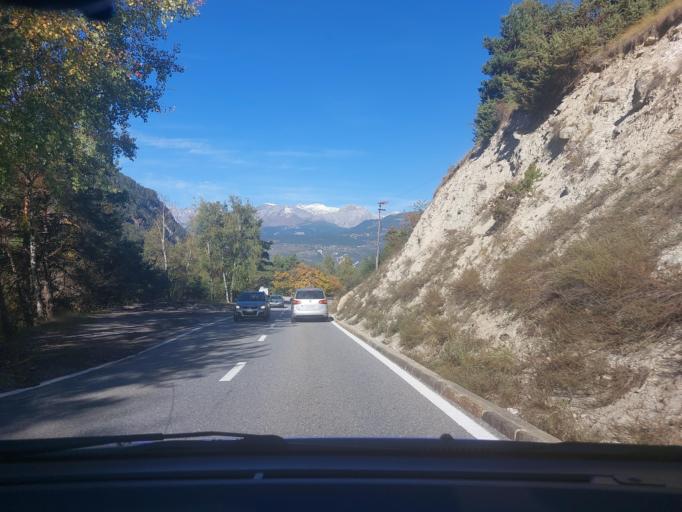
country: CH
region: Valais
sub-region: Sierre District
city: Chippis
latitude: 46.2589
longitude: 7.5669
